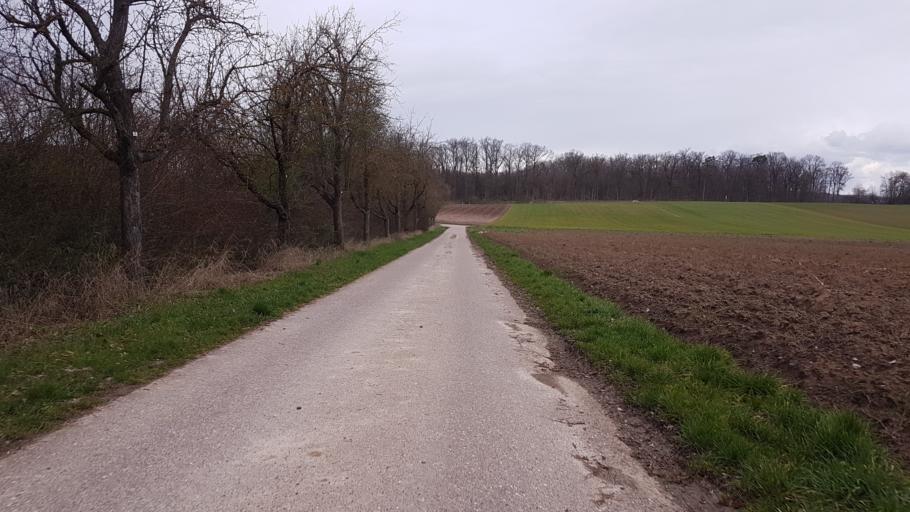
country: DE
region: Baden-Wuerttemberg
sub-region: Regierungsbezirk Stuttgart
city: Brackenheim
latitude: 49.0940
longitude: 9.0938
